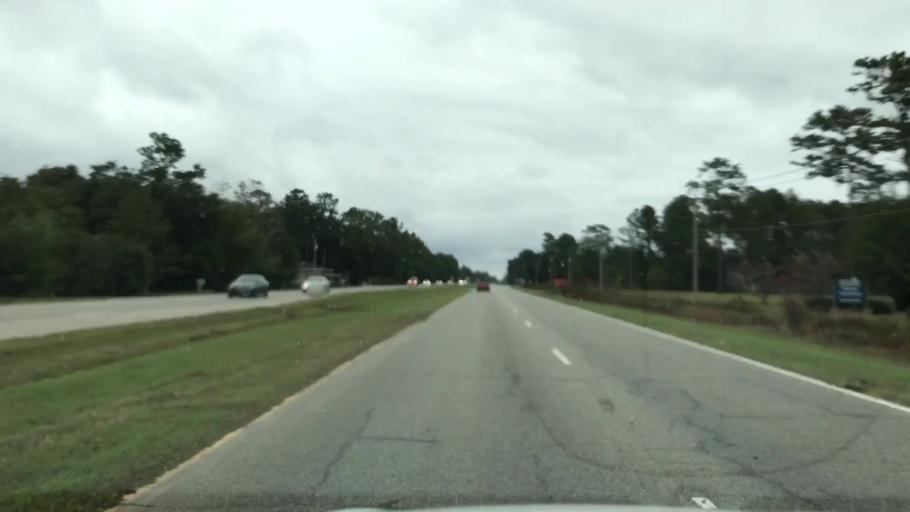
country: US
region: South Carolina
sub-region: Georgetown County
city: Georgetown
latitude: 33.3180
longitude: -79.3245
